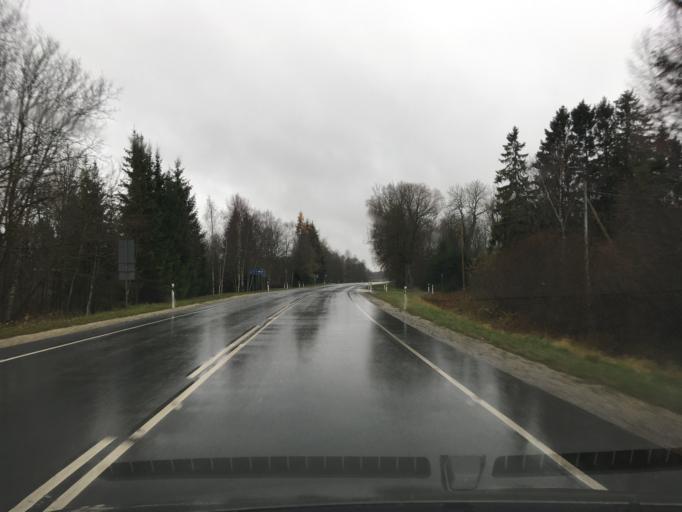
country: EE
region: Laeaene
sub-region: Lihula vald
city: Lihula
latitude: 58.8183
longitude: 24.0569
